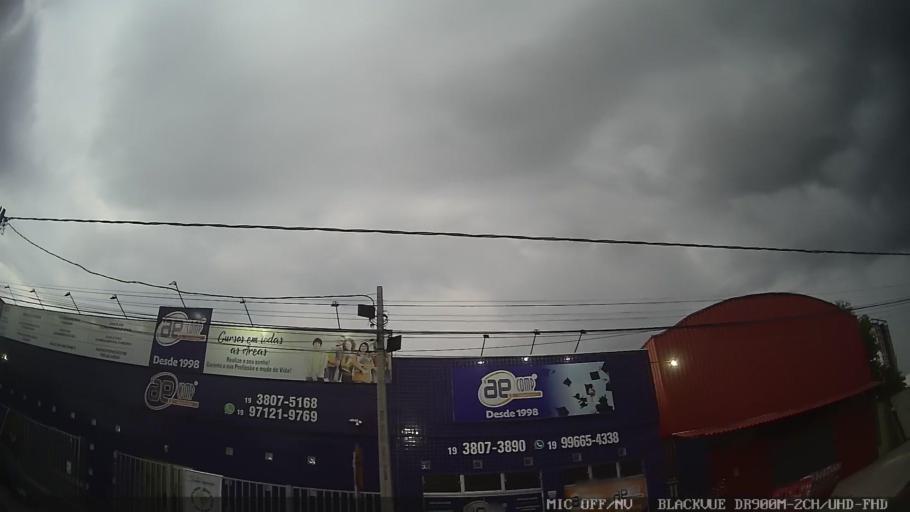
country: BR
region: Sao Paulo
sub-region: Amparo
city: Amparo
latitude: -22.7098
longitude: -46.7751
